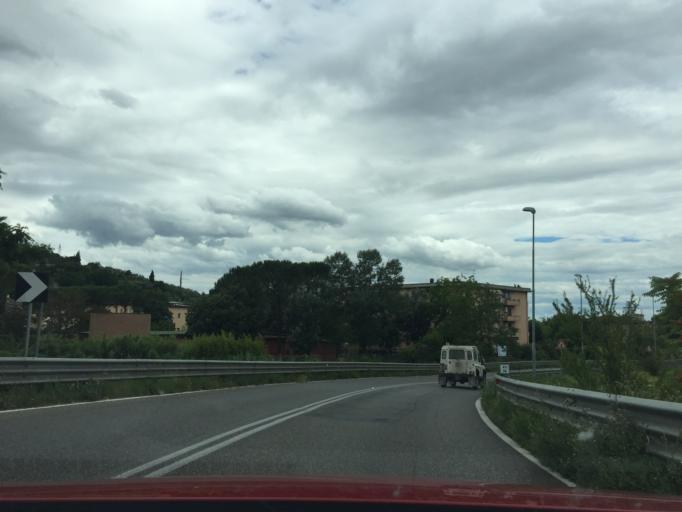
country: IT
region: Tuscany
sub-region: Province of Florence
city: Montelupo Fiorentino
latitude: 43.7271
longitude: 11.0243
